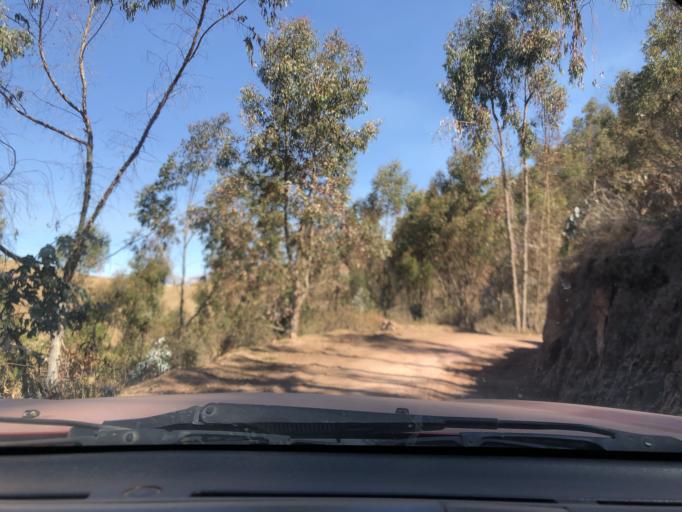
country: PE
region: Ayacucho
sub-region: Provincia de La Mar
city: Chilcas
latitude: -13.1842
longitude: -73.8420
